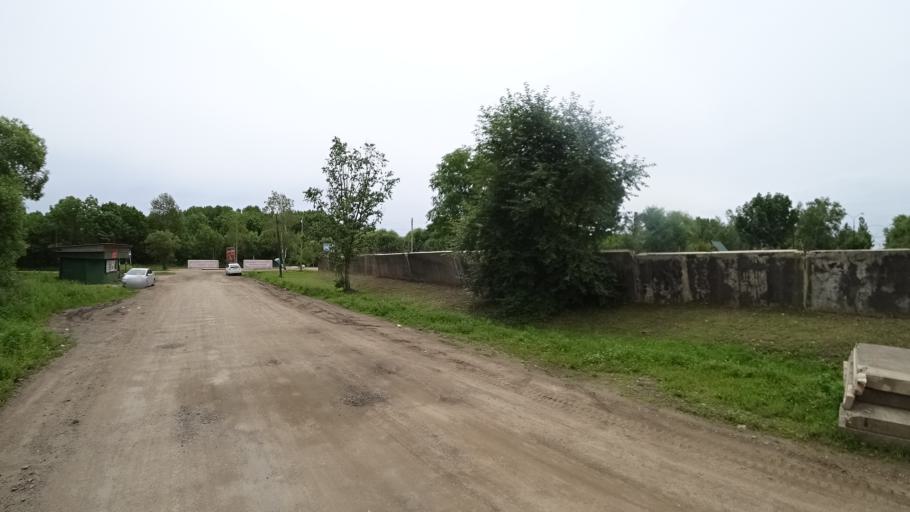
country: RU
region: Primorskiy
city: Novosysoyevka
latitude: 44.2013
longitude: 133.3170
